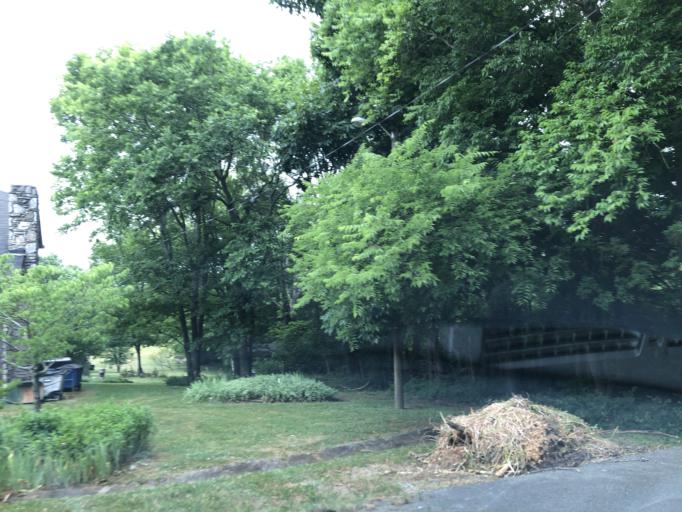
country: US
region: Tennessee
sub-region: Davidson County
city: Goodlettsville
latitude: 36.2858
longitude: -86.7335
